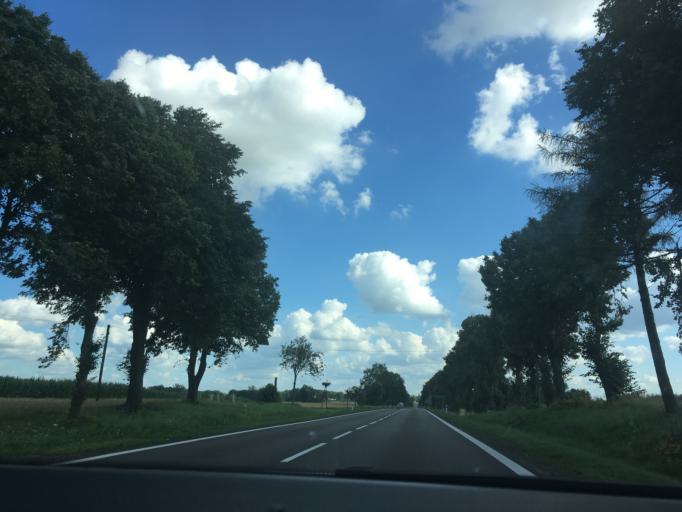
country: PL
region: Podlasie
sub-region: Powiat sokolski
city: Janow
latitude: 53.4240
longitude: 23.1085
